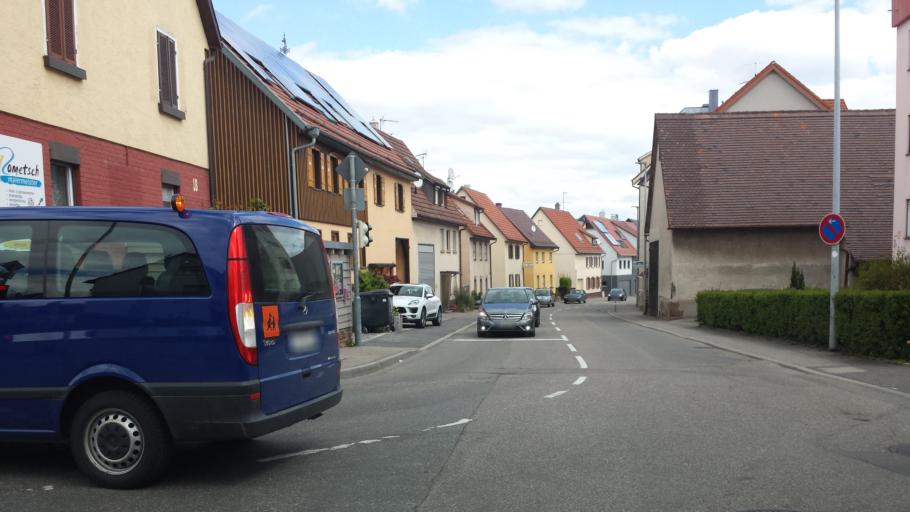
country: DE
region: Baden-Wuerttemberg
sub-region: Regierungsbezirk Stuttgart
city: Gerlingen
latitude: 48.8002
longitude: 9.0595
